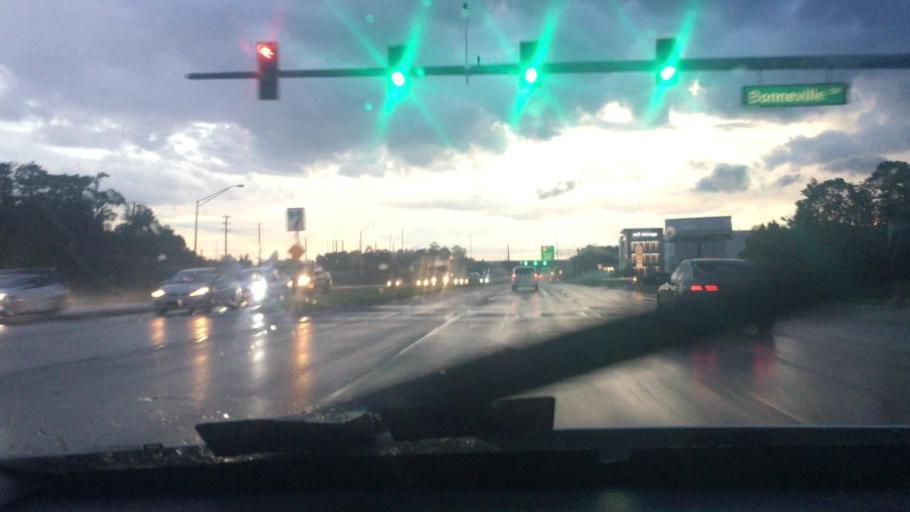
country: US
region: Florida
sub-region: Orange County
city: Alafaya
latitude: 28.5654
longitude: -81.1871
